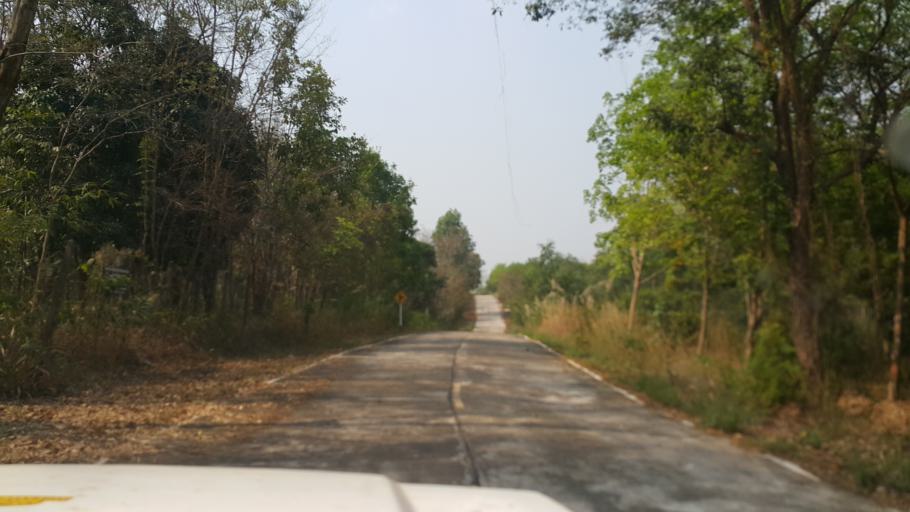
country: TH
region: Nakhon Phanom
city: Ban Phaeng
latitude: 17.9727
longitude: 104.1513
